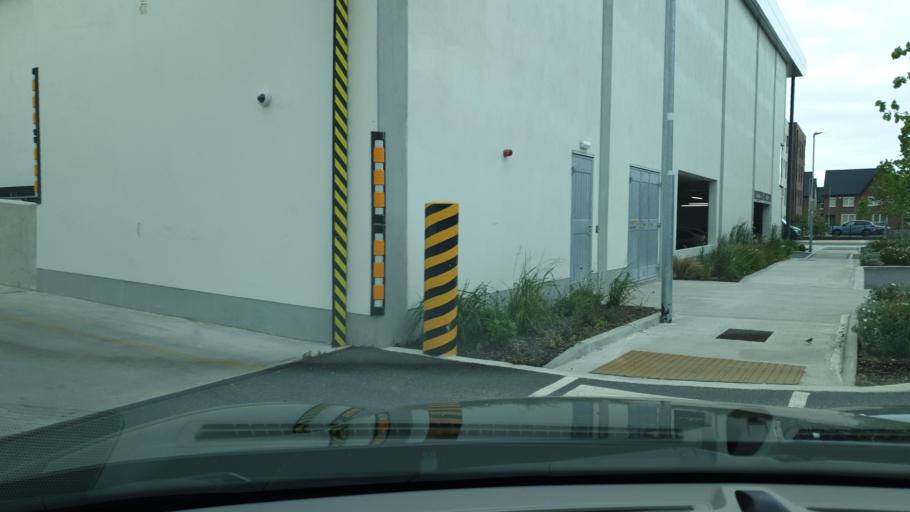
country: IE
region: Leinster
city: Lucan
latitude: 53.3455
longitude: -6.4747
